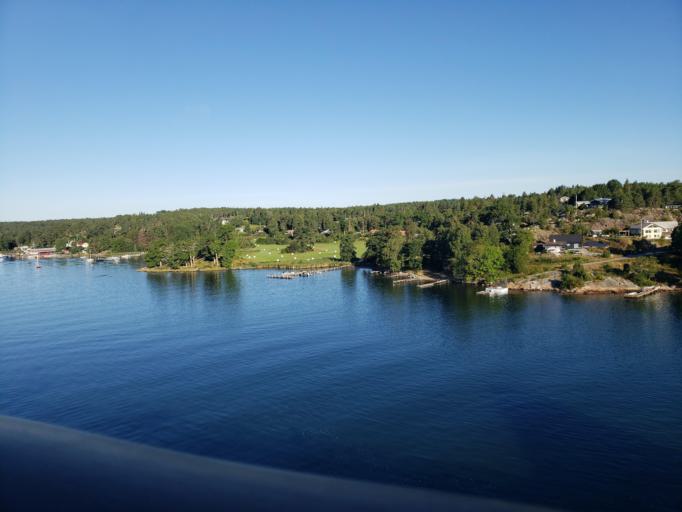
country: SE
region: Stockholm
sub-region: Vaxholms Kommun
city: Vaxholm
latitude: 59.5039
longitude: 18.4756
